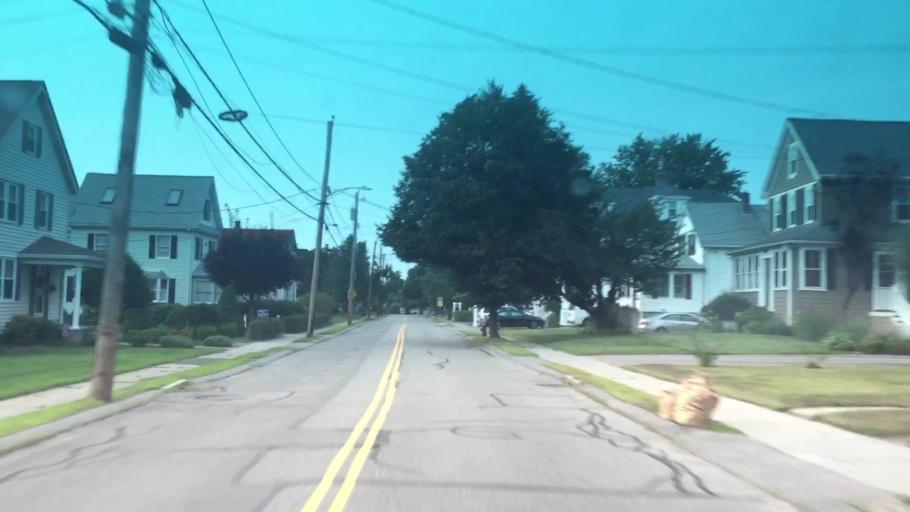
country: US
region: Massachusetts
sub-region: Norfolk County
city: Norwood
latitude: 42.1979
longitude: -71.1957
